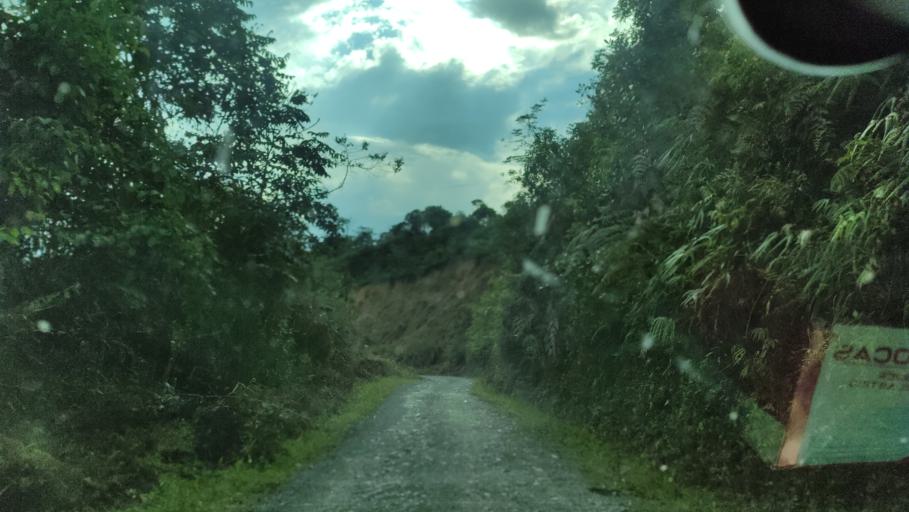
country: CO
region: Valle del Cauca
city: San Pedro
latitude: 3.8779
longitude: -76.1600
